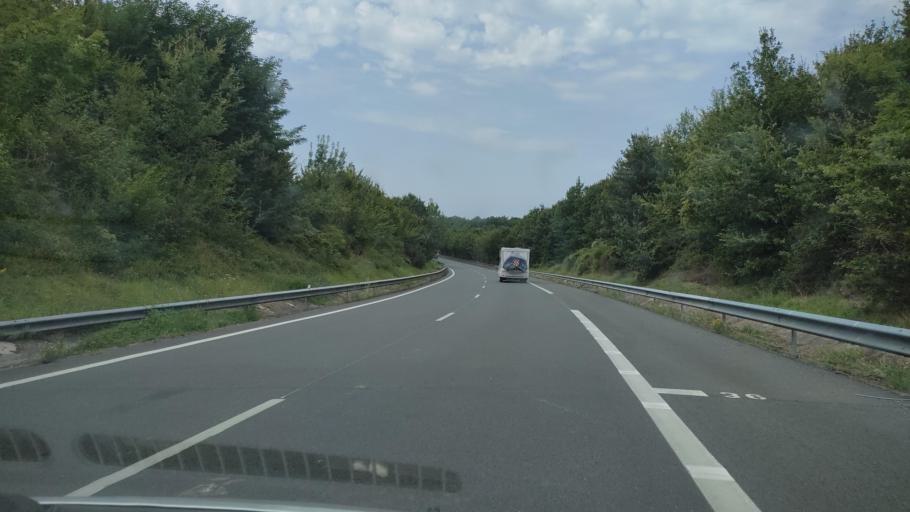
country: FR
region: Poitou-Charentes
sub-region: Departement de la Charente-Maritime
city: Bussac-sur-Charente
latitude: 45.7942
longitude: -0.6647
